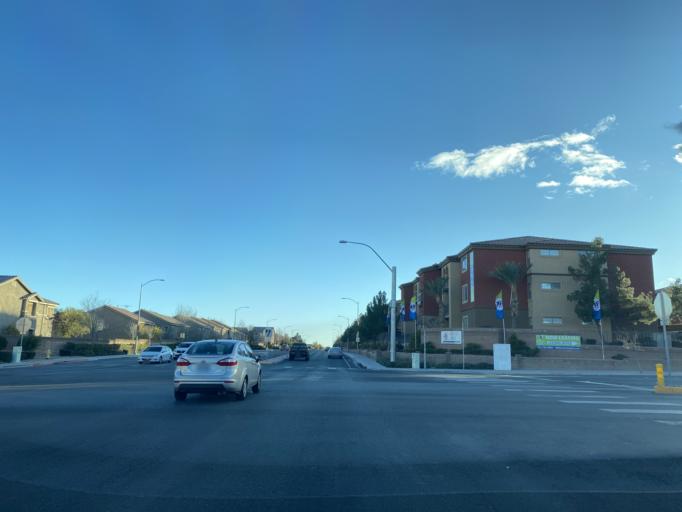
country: US
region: Nevada
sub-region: Clark County
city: Summerlin South
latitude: 36.3069
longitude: -115.3059
